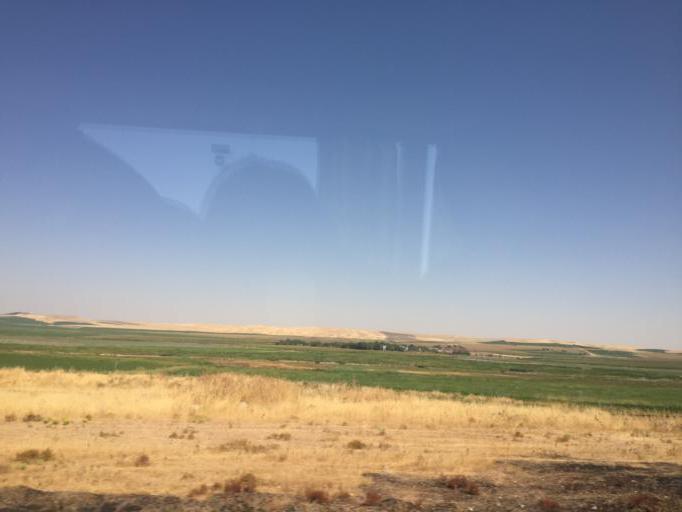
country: TR
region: Diyarbakir
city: Tepe
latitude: 37.8485
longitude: 40.7975
